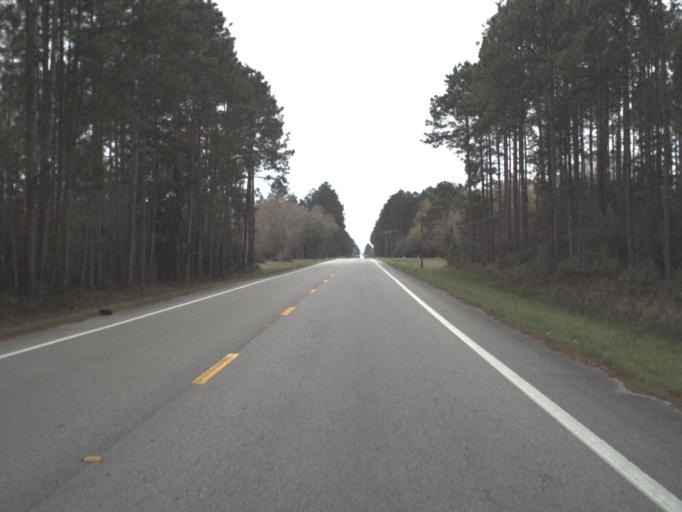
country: US
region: Florida
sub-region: Gulf County
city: Wewahitchka
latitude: 29.9579
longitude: -85.1774
